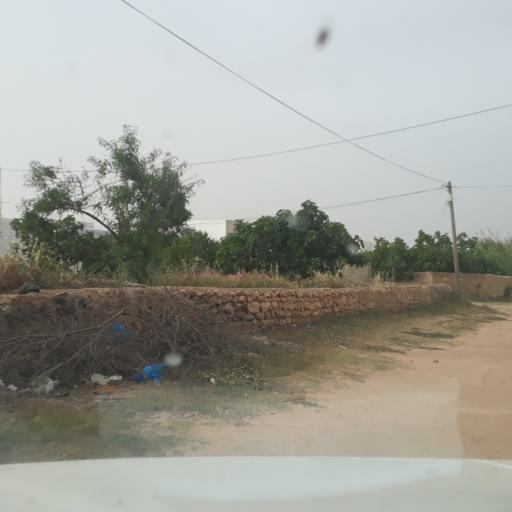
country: TN
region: Safaqis
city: Al Qarmadah
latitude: 34.8191
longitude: 10.7723
